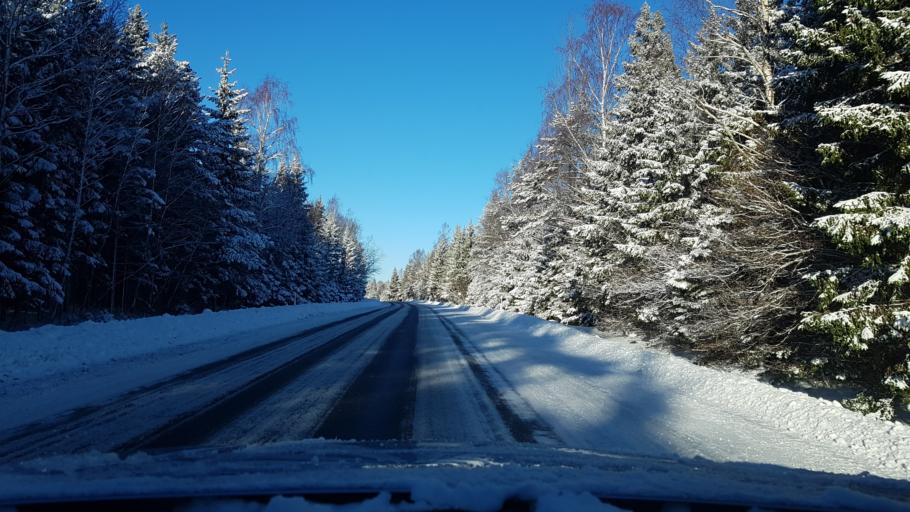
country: EE
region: Hiiumaa
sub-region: Kaerdla linn
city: Kardla
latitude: 58.9744
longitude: 22.8201
